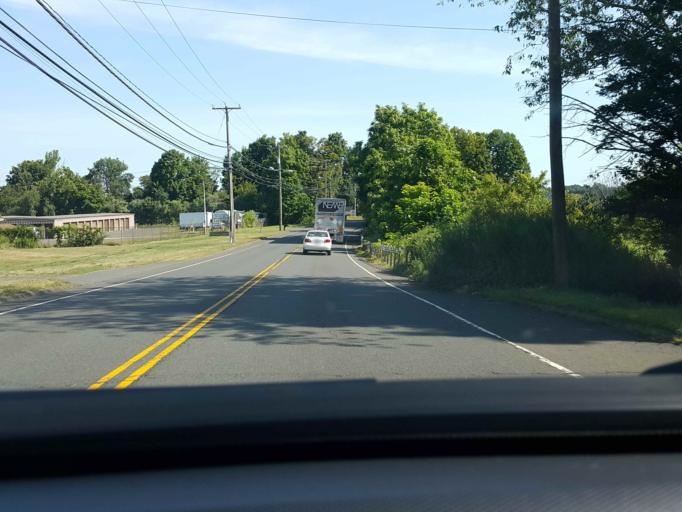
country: US
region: Connecticut
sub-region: Middlesex County
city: Durham
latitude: 41.5054
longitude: -72.6721
